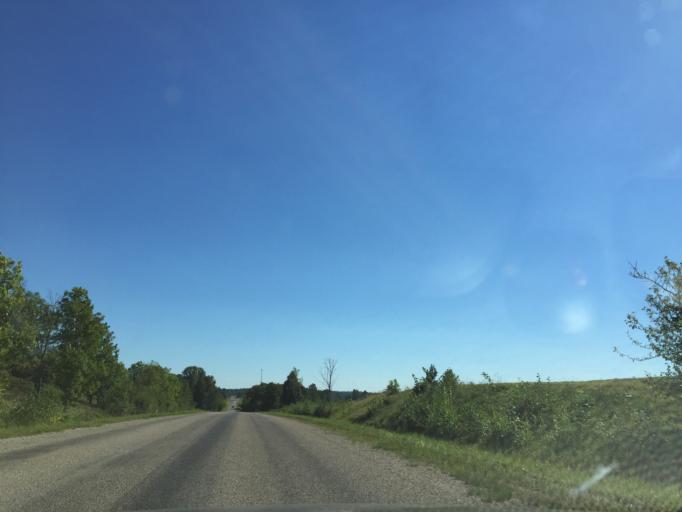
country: LV
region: Akniste
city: Akniste
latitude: 56.0292
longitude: 25.9149
